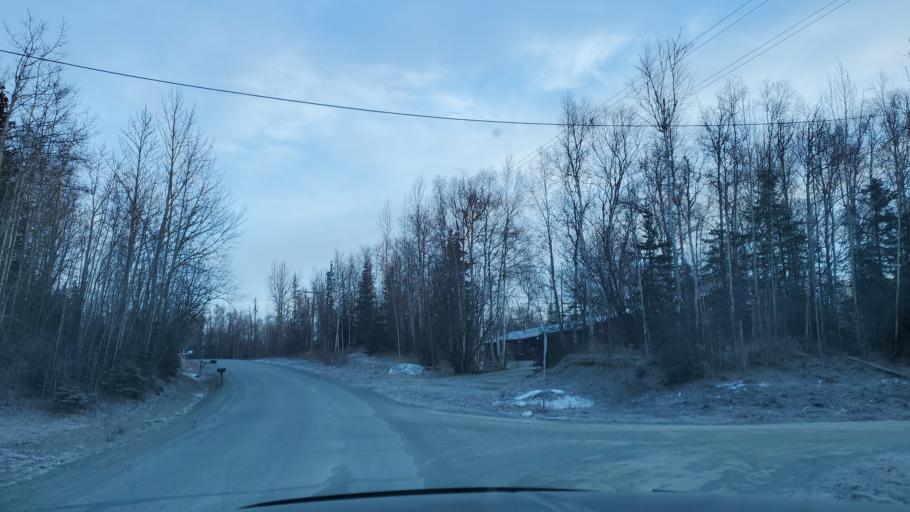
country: US
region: Alaska
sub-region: Matanuska-Susitna Borough
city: Lakes
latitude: 61.6049
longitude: -149.3174
